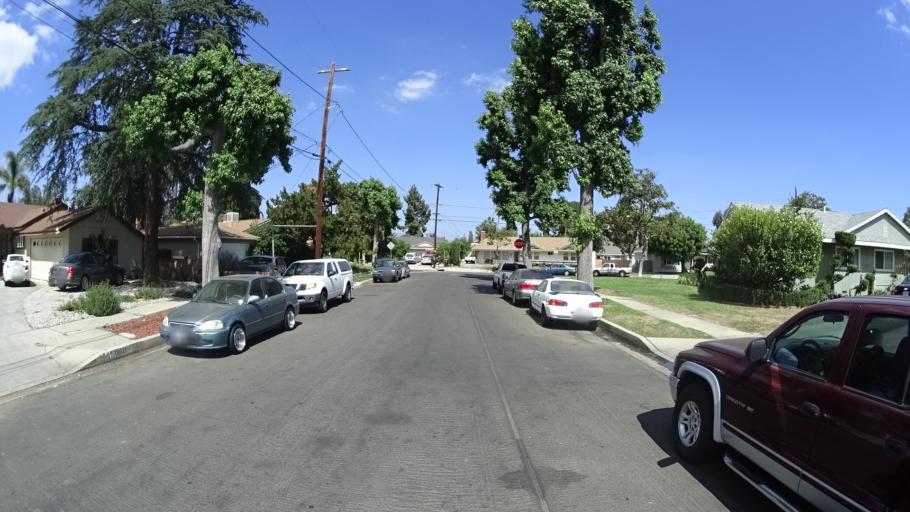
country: US
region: California
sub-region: Los Angeles County
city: Van Nuys
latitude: 34.2337
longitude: -118.4597
